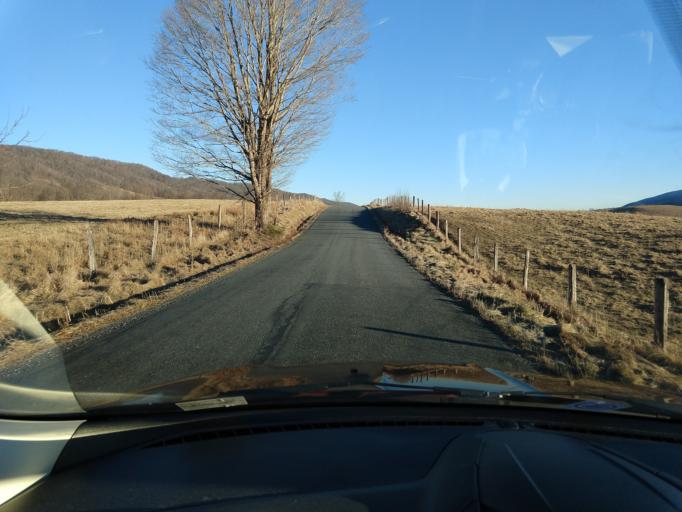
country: US
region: Virginia
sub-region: Highland County
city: Monterey
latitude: 38.3796
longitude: -79.6641
